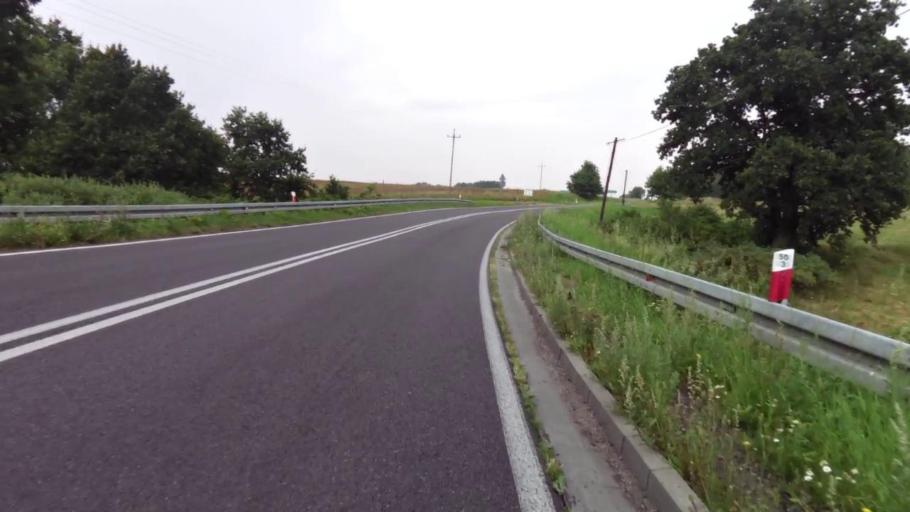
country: PL
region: West Pomeranian Voivodeship
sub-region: Powiat lobeski
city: Wegorzyno
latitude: 53.5068
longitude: 15.6498
